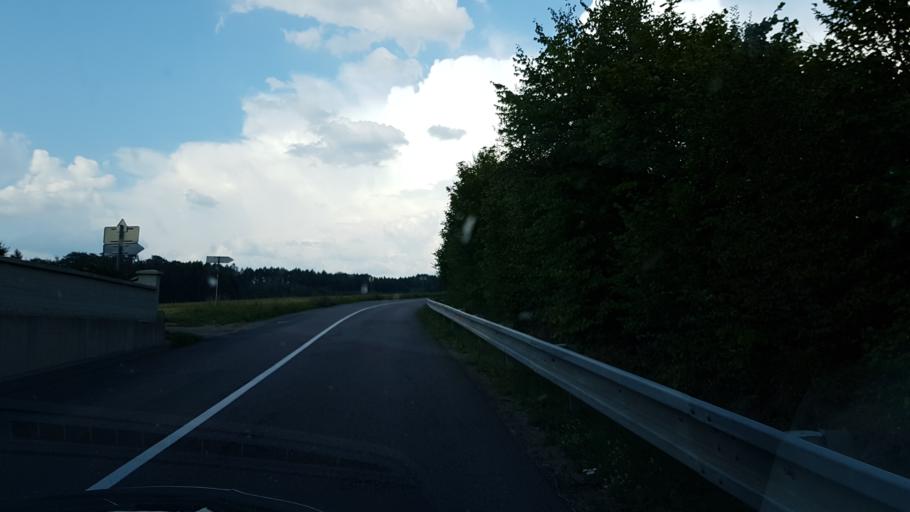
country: CZ
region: Pardubicky
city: Lukavice
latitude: 50.0801
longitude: 16.5093
